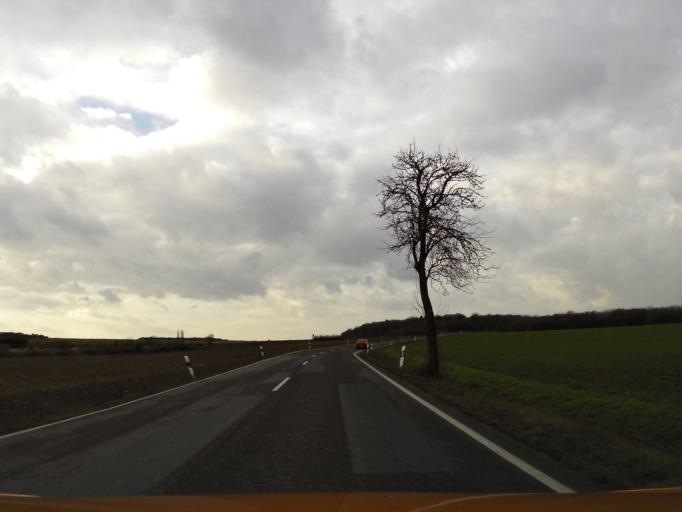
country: DE
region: Saxony-Anhalt
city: Beendorf
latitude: 52.2889
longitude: 11.1035
